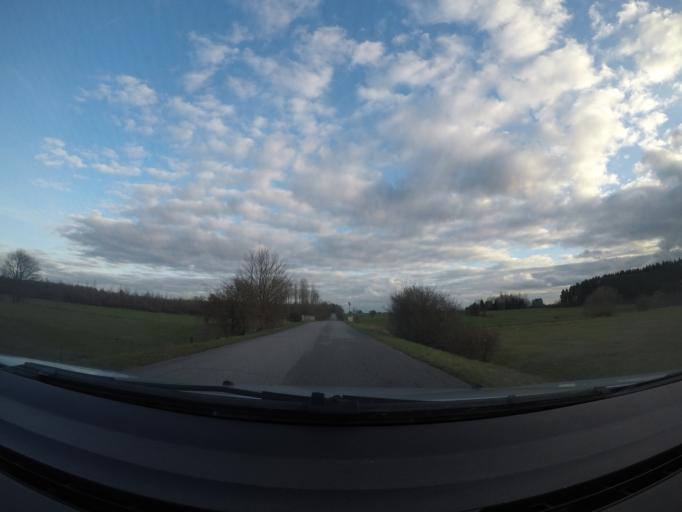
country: BE
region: Wallonia
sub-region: Province du Luxembourg
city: Etalle
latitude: 49.6856
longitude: 5.5634
